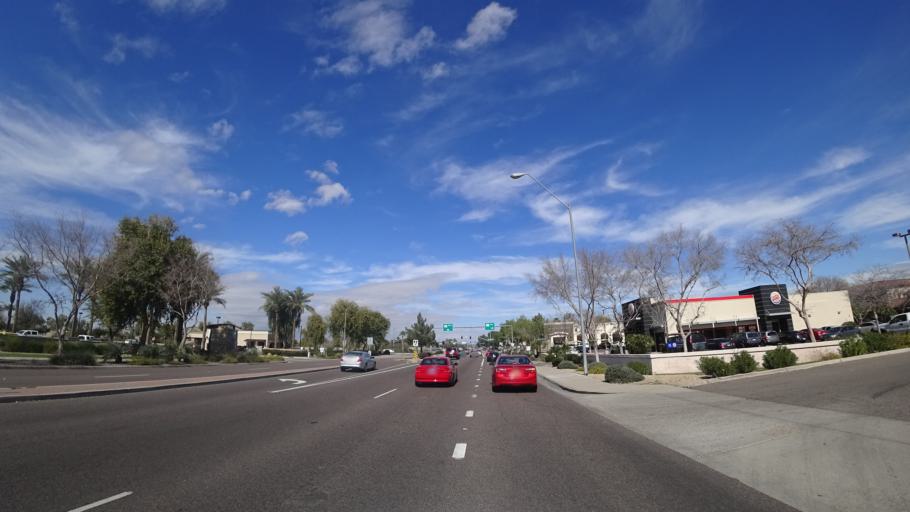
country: US
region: Arizona
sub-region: Maricopa County
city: Peoria
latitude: 33.6661
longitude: -112.2029
